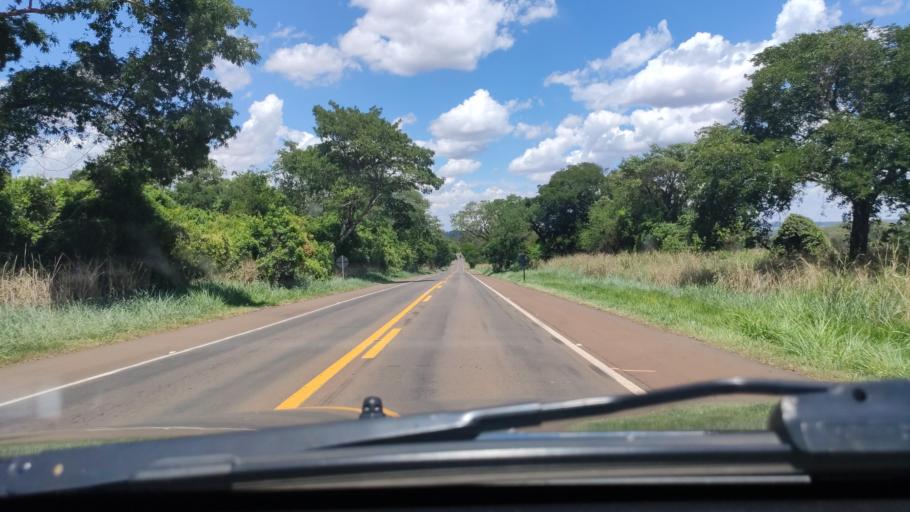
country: BR
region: Sao Paulo
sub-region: Boa Esperanca Do Sul
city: Boa Esperanca do Sul
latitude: -22.0696
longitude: -48.4124
